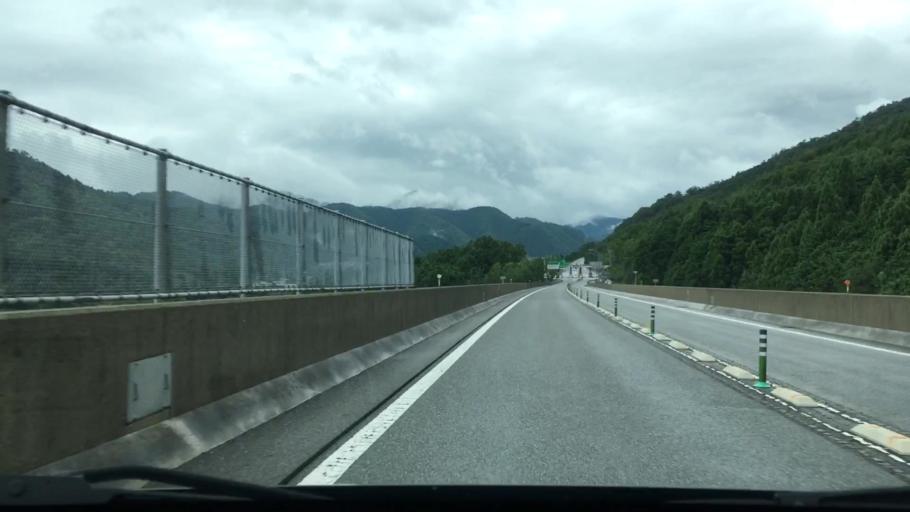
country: JP
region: Hyogo
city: Toyooka
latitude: 35.2908
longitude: 134.8241
